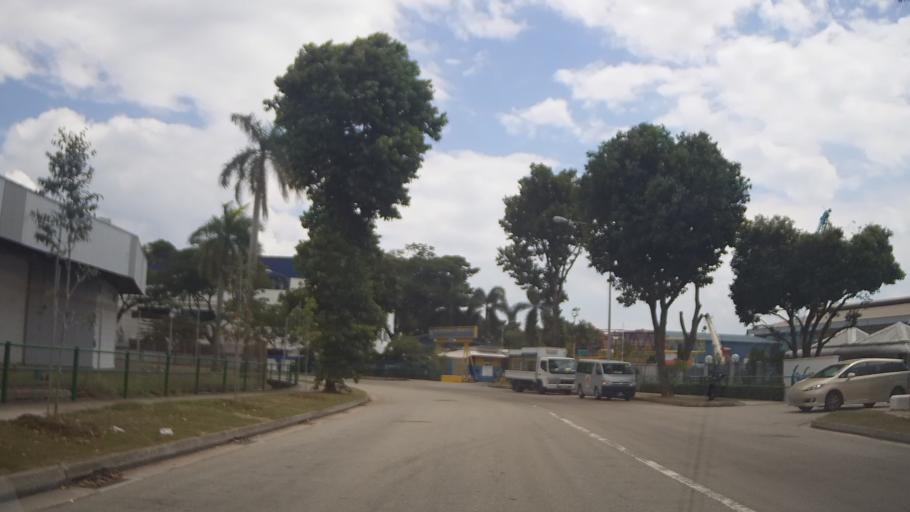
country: SG
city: Singapore
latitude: 1.3025
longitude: 103.7597
